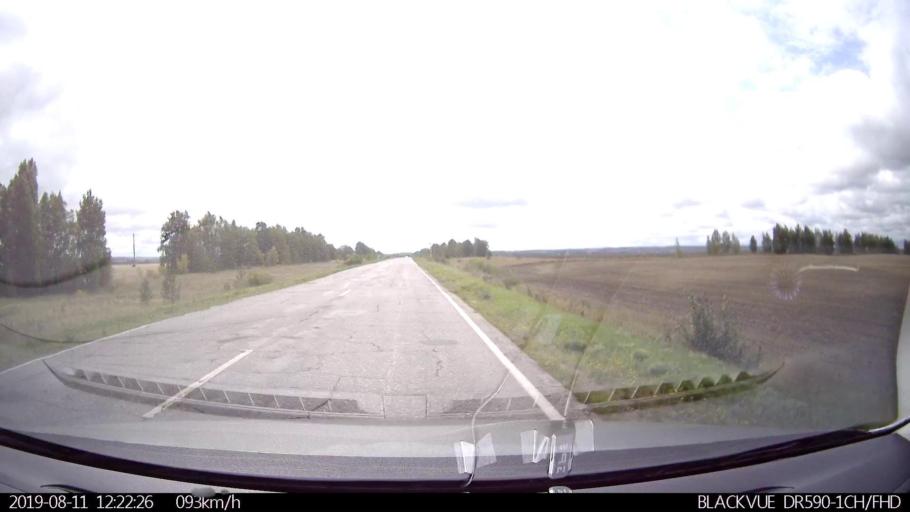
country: RU
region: Ulyanovsk
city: Ignatovka
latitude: 53.9076
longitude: 47.9542
